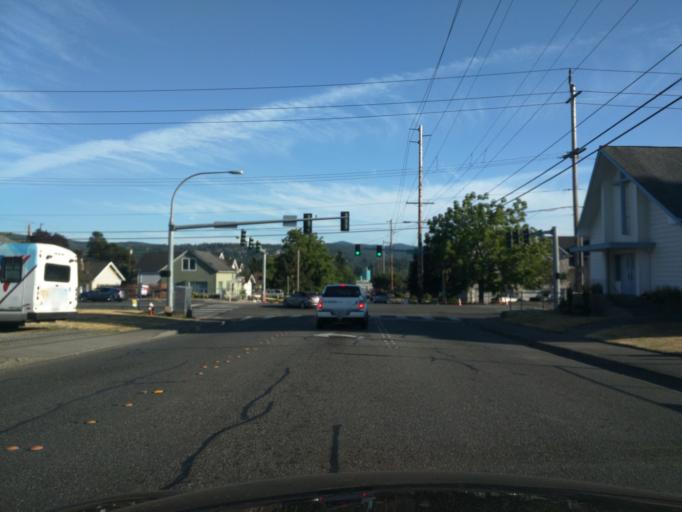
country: US
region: Washington
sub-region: Whatcom County
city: Bellingham
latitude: 48.7635
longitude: -122.4577
